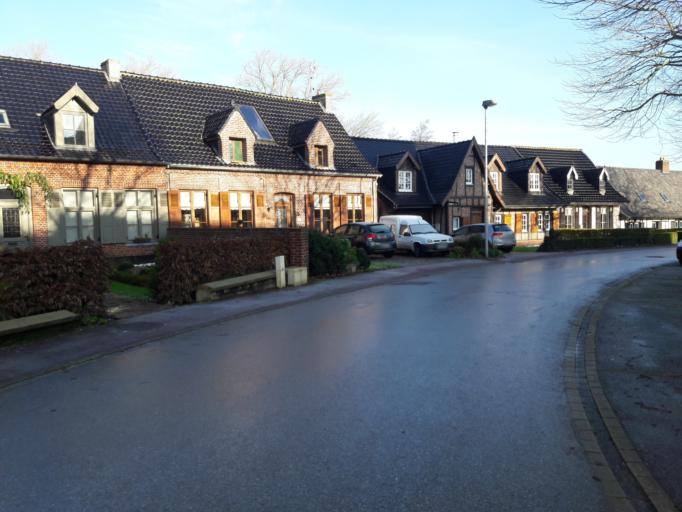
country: FR
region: Nord-Pas-de-Calais
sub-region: Departement du Nord
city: Saint-Sylvestre-Cappel
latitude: 50.7990
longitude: 2.5385
